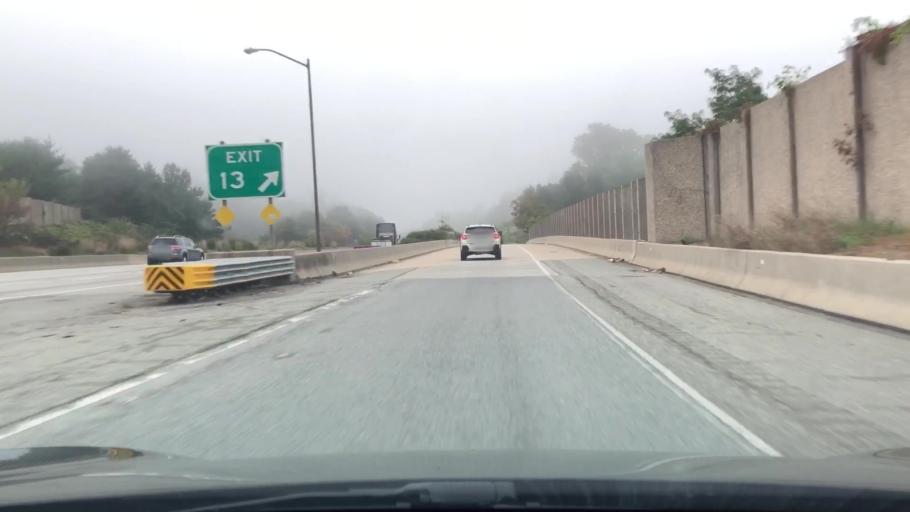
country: US
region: Pennsylvania
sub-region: Delaware County
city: Radnor
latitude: 40.0372
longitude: -75.3552
